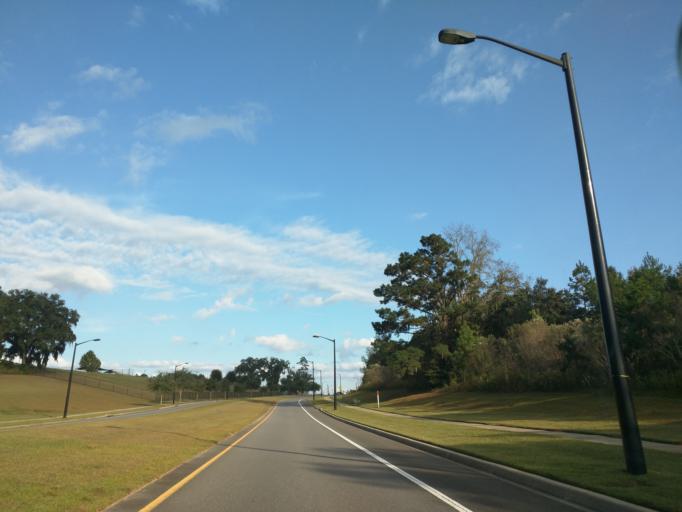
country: US
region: Florida
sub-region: Leon County
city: Tallahassee
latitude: 30.4122
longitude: -84.2272
